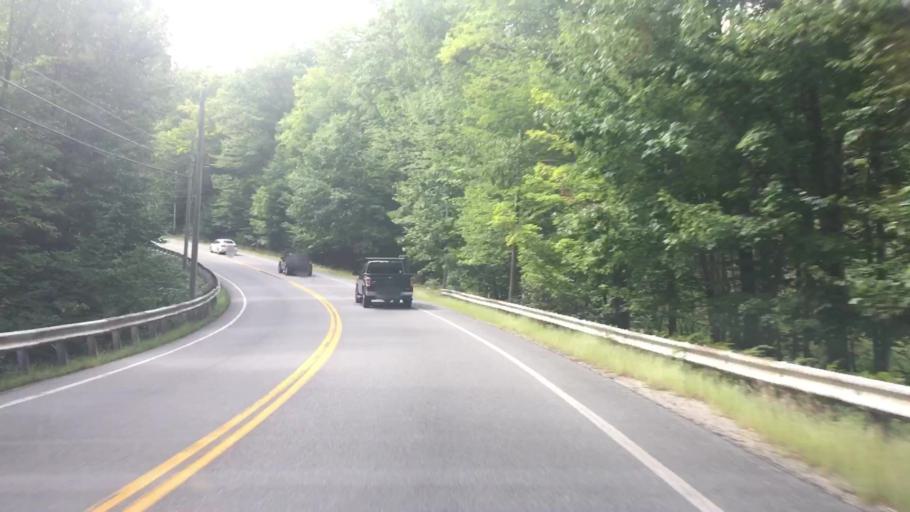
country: US
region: Maine
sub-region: Cumberland County
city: Raymond
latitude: 43.9857
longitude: -70.4937
